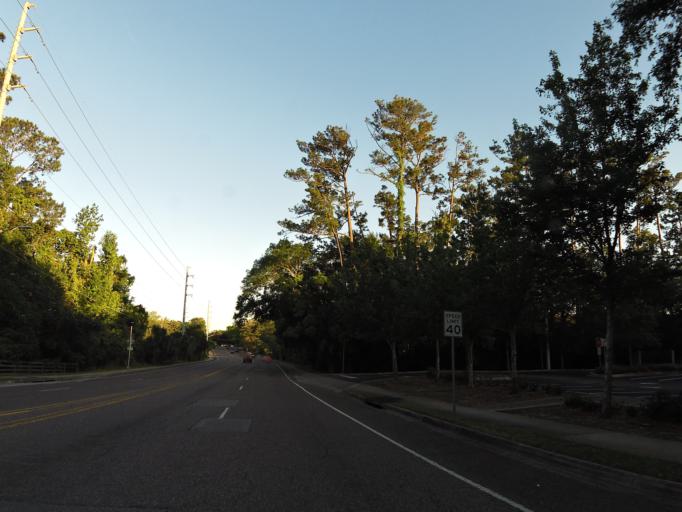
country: US
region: Florida
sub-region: Duval County
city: Jacksonville
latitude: 30.3248
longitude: -81.5844
